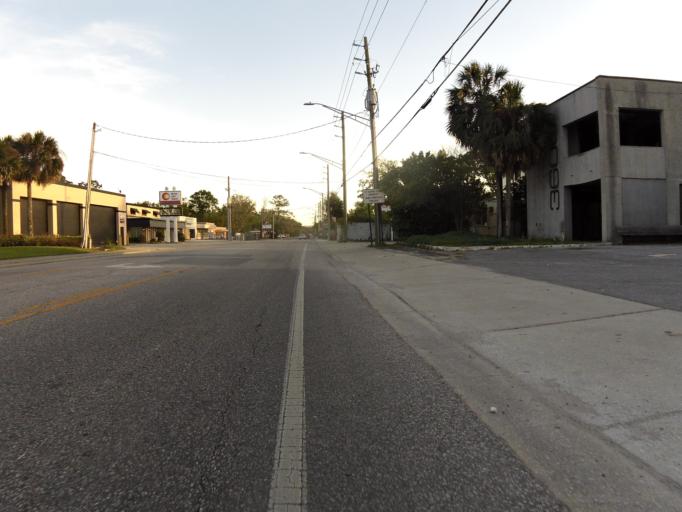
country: US
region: Florida
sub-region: Duval County
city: Jacksonville
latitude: 30.2872
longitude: -81.6439
